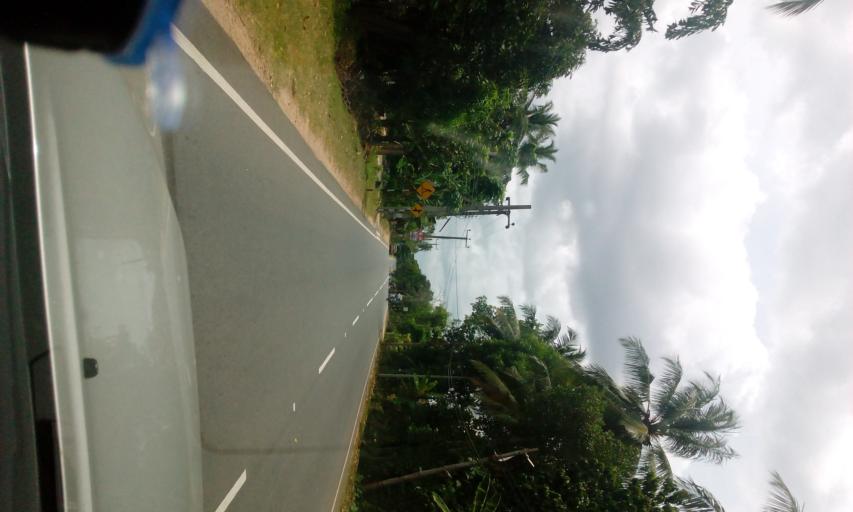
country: LK
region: North Western
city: Kuliyapitiya
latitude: 7.4523
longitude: 80.1630
